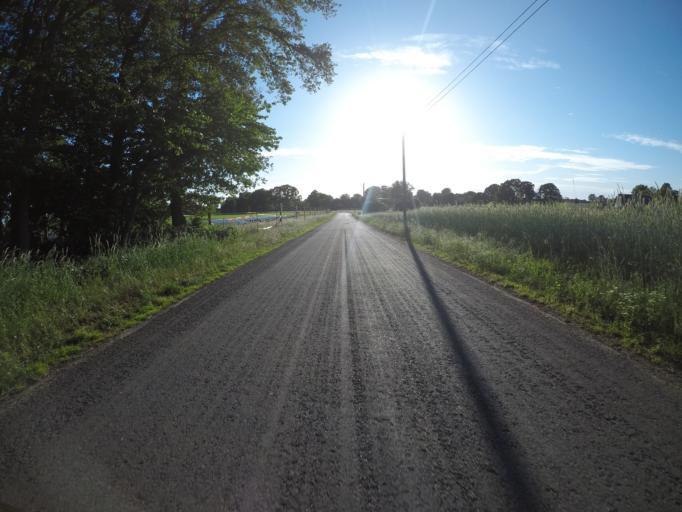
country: DE
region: North Rhine-Westphalia
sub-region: Regierungsbezirk Dusseldorf
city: Schermbeck
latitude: 51.7197
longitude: 6.8779
